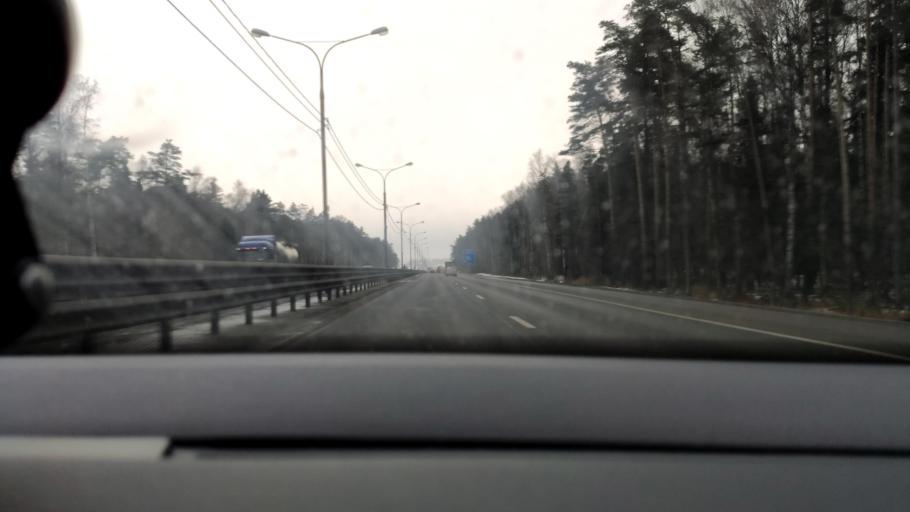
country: RU
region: Moskovskaya
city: Kostino
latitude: 56.0358
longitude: 37.8900
